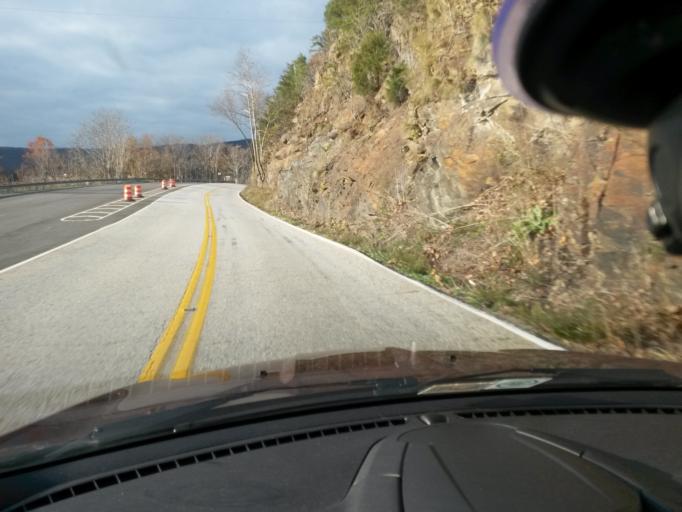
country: US
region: Virginia
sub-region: Rockbridge County
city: Glasgow
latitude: 37.5919
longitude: -79.3797
